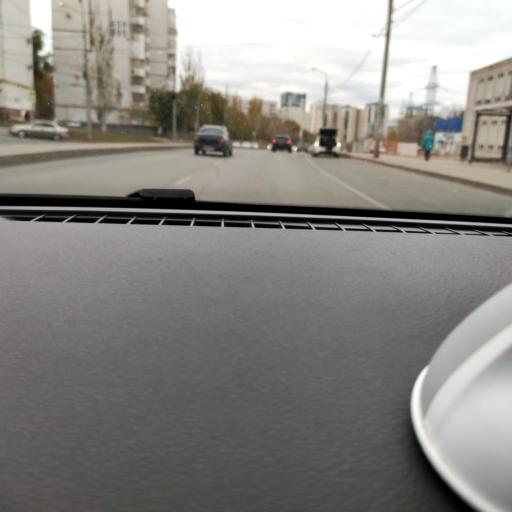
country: RU
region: Samara
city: Samara
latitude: 53.2467
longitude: 50.1958
